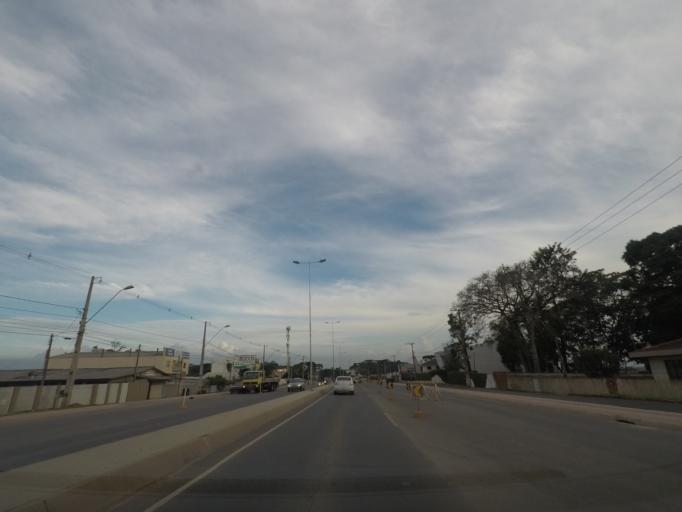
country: BR
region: Parana
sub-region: Colombo
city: Colombo
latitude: -25.3139
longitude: -49.2210
